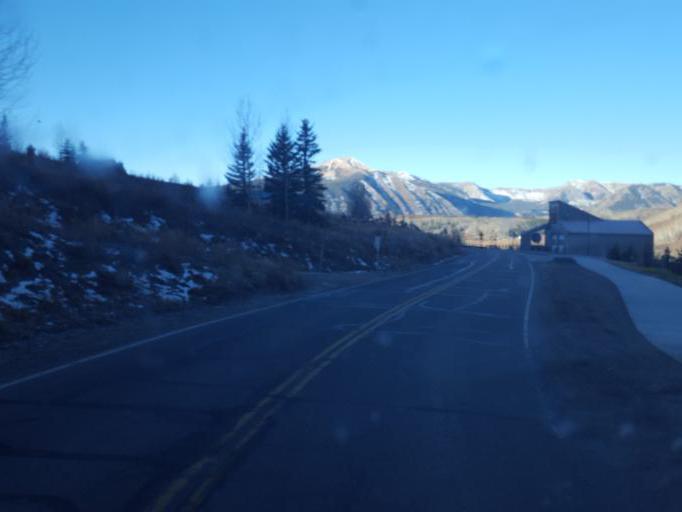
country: US
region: Colorado
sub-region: Gunnison County
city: Crested Butte
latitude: 38.9120
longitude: -106.9640
